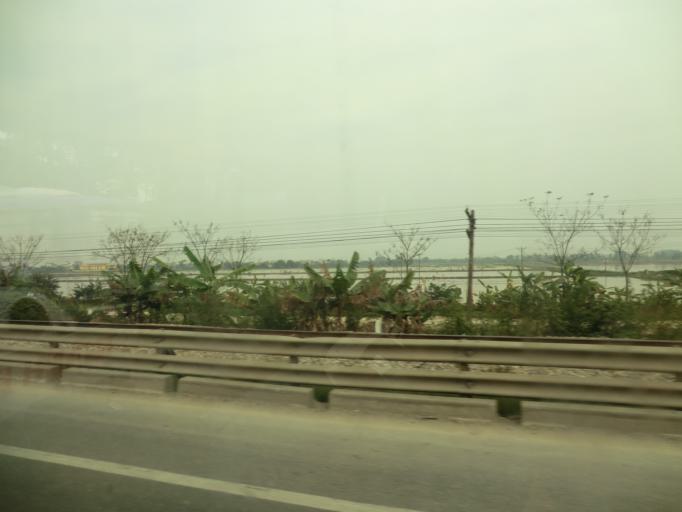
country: VN
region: Ha Noi
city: Phu Xuyen
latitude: 20.6871
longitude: 105.9119
